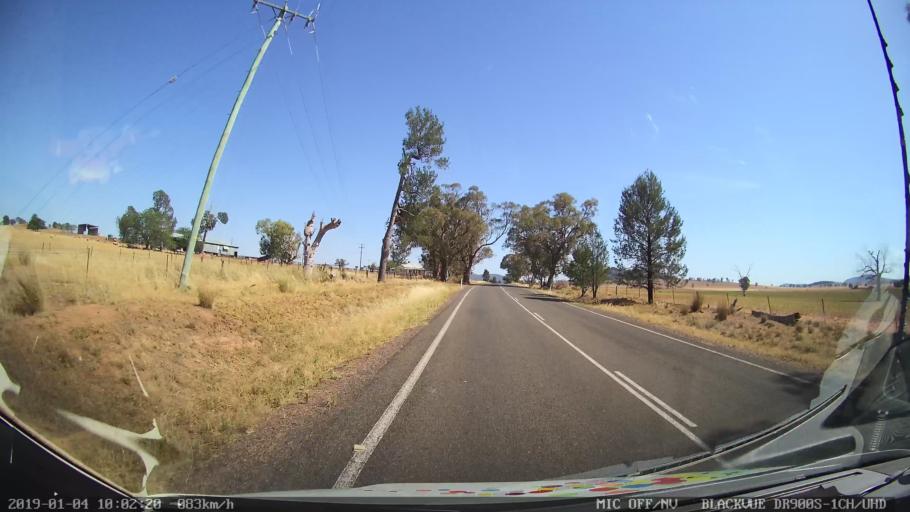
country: AU
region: New South Wales
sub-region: Cabonne
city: Canowindra
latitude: -33.4775
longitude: 148.3656
